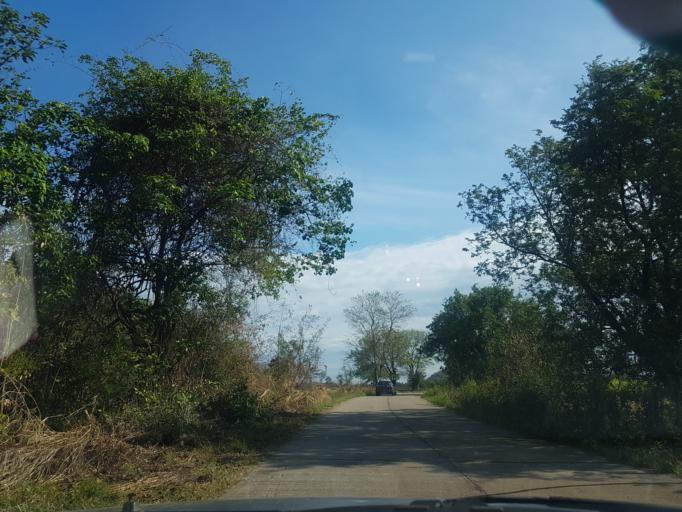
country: TH
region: Lop Buri
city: Lop Buri
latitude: 14.8230
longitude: 100.7550
